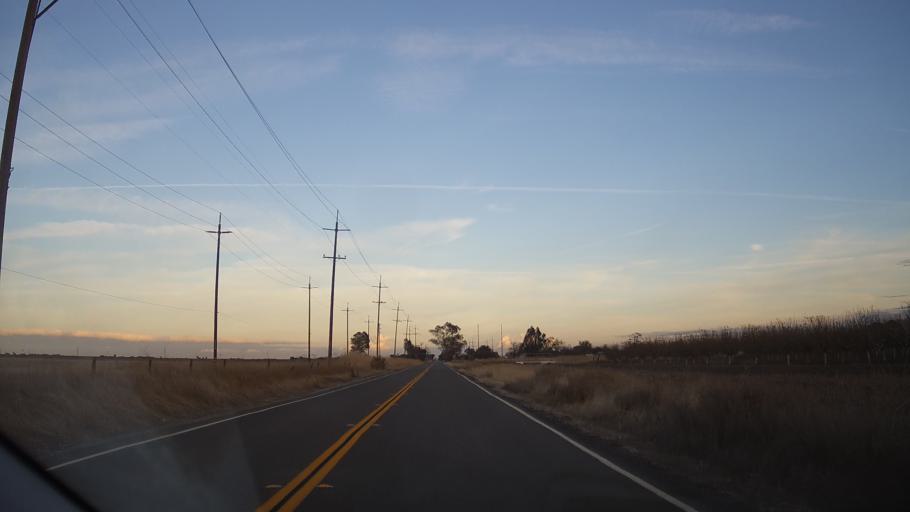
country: US
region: California
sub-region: Solano County
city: Hartley
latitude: 38.4025
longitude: -121.9111
